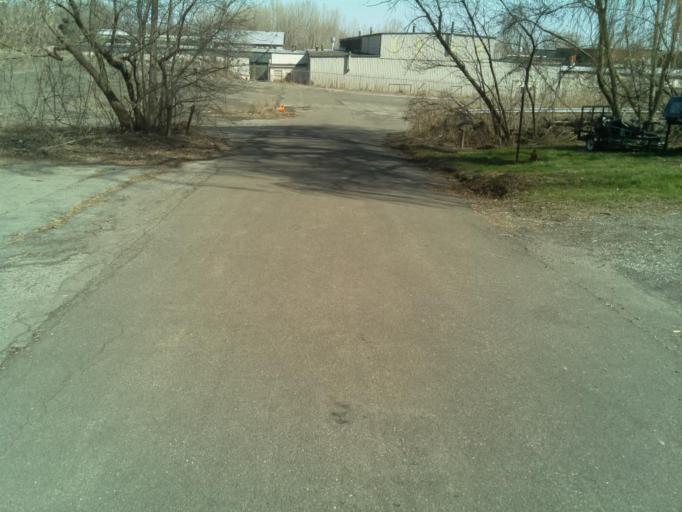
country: US
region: New York
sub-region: Onondaga County
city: East Syracuse
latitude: 43.0715
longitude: -76.1016
